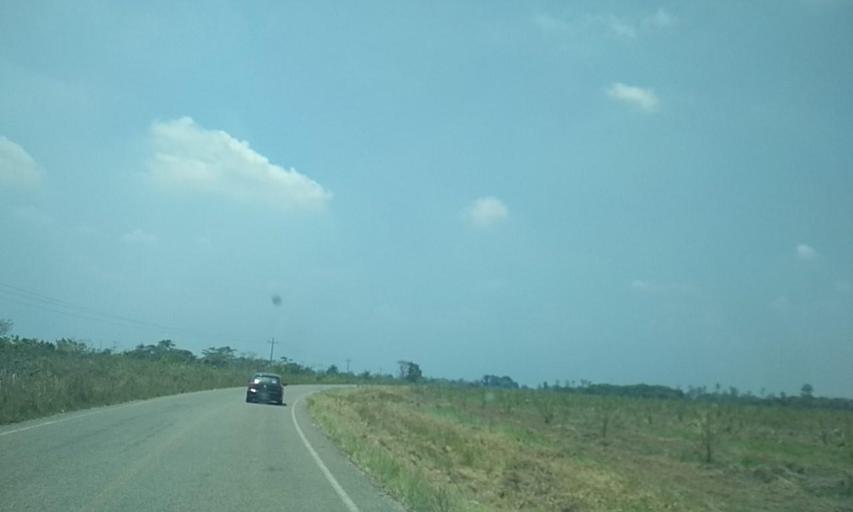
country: MX
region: Tabasco
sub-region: Huimanguillo
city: Paso de la Mina 3ra. Seccion
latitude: 17.8257
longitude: -93.6173
